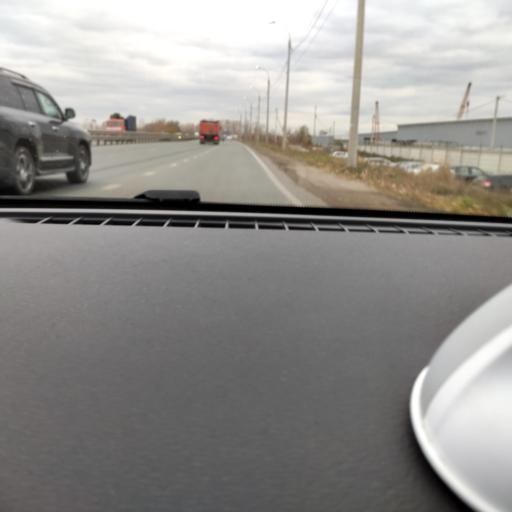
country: RU
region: Samara
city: Samara
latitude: 53.0973
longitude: 50.1582
